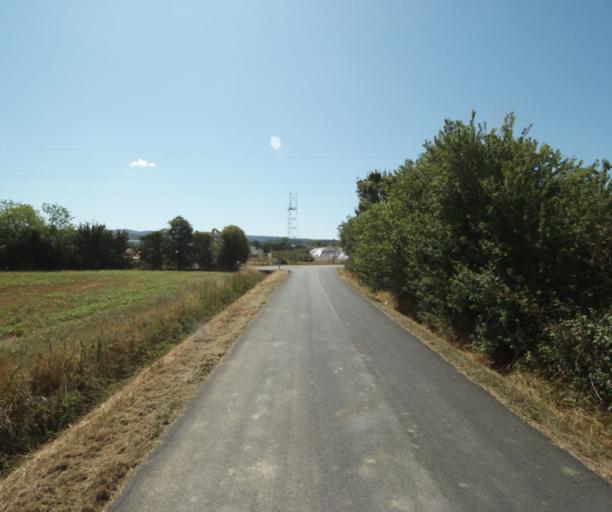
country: FR
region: Midi-Pyrenees
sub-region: Departement de la Haute-Garonne
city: Revel
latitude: 43.4570
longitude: 1.9740
